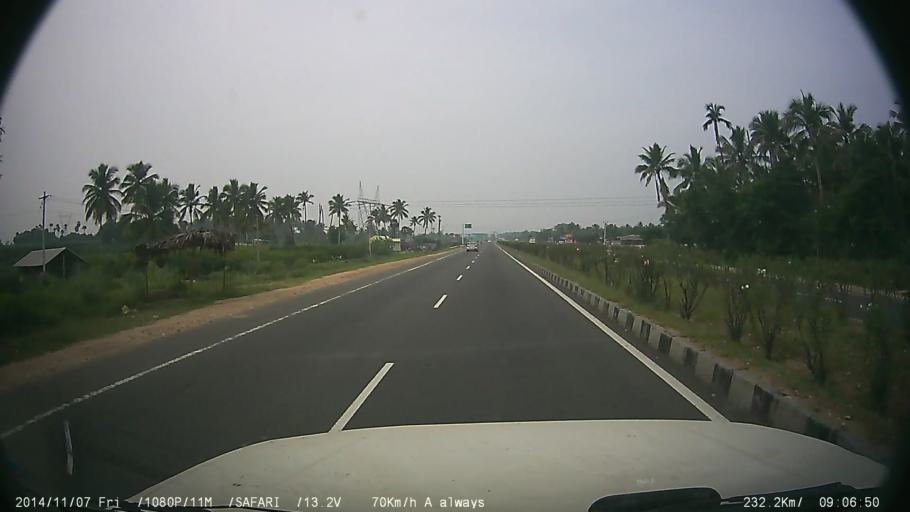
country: IN
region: Tamil Nadu
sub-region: Salem
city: Konganapuram
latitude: 11.5180
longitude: 77.9318
